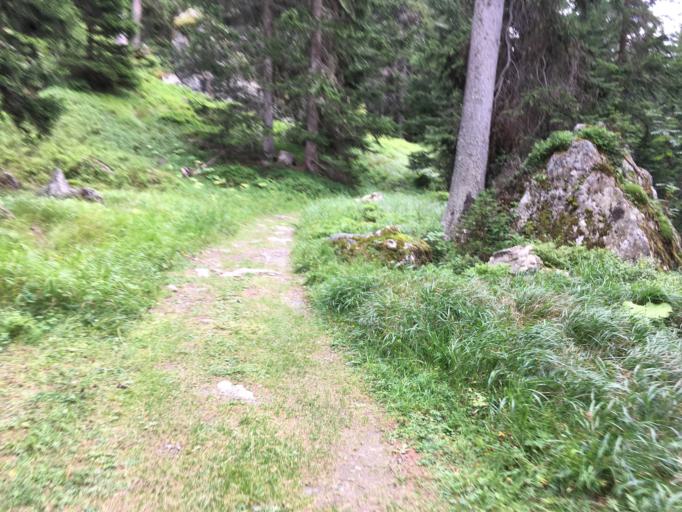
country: CH
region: Grisons
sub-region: Maloja District
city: Silvaplana
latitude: 46.4827
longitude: 9.6486
